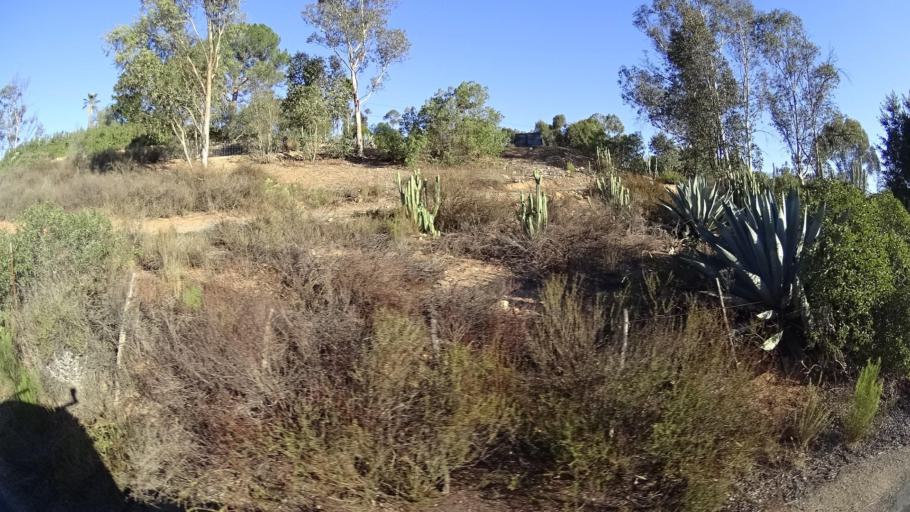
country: US
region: California
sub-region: San Diego County
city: Jamul
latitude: 32.7042
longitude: -116.8914
